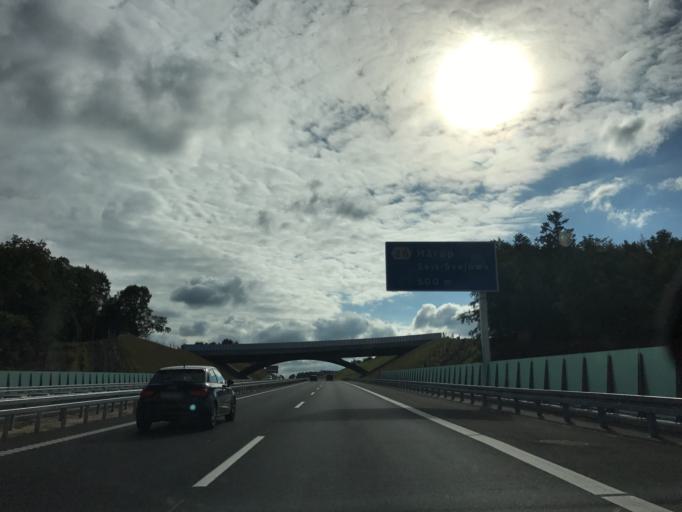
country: DK
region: Central Jutland
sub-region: Silkeborg Kommune
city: Svejbaek
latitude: 56.1579
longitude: 9.6196
